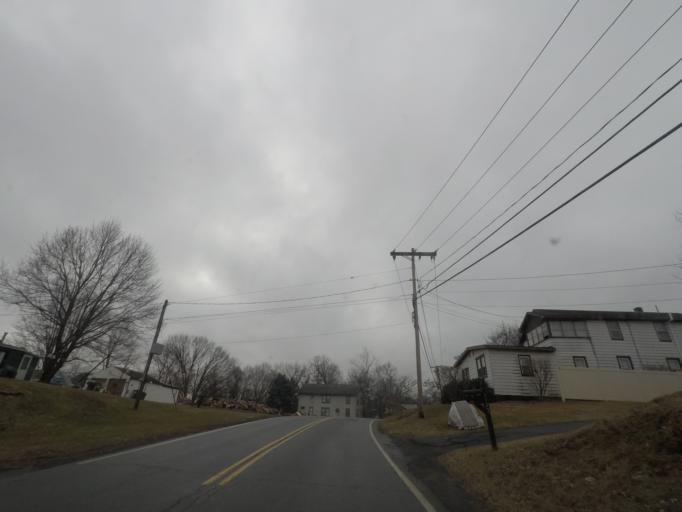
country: US
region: New York
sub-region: Saratoga County
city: Waterford
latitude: 42.7962
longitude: -73.6668
